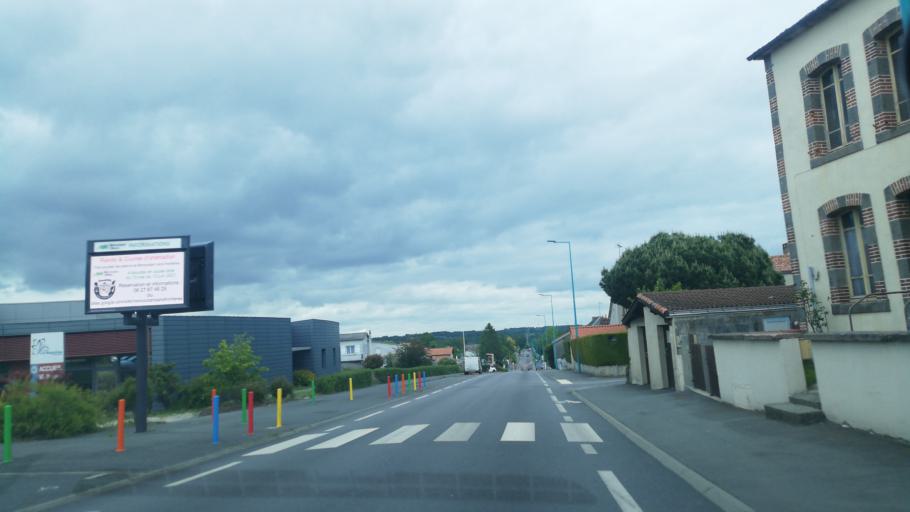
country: FR
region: Poitou-Charentes
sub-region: Departement des Deux-Sevres
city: Moncoutant
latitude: 46.7253
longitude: -0.5877
